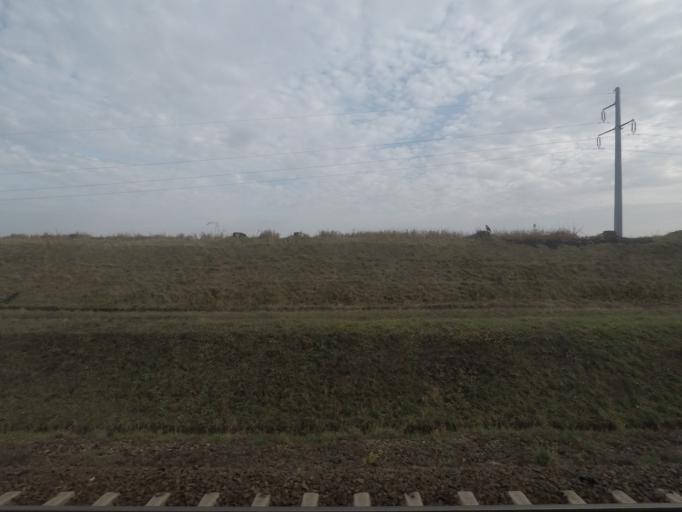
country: PL
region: Subcarpathian Voivodeship
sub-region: Powiat jaroslawski
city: Sosnica
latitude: 49.8635
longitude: 22.8576
